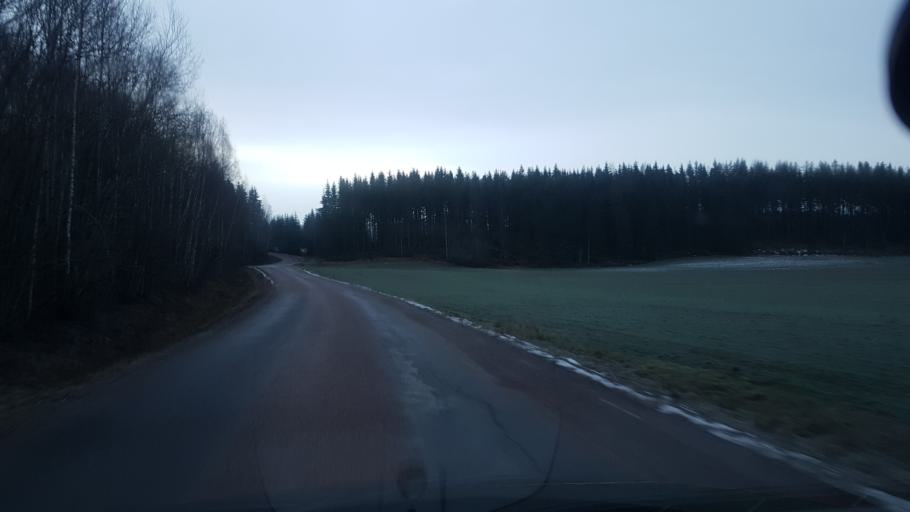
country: SE
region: Dalarna
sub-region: Borlange Kommun
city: Ornas
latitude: 60.4396
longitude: 15.6479
